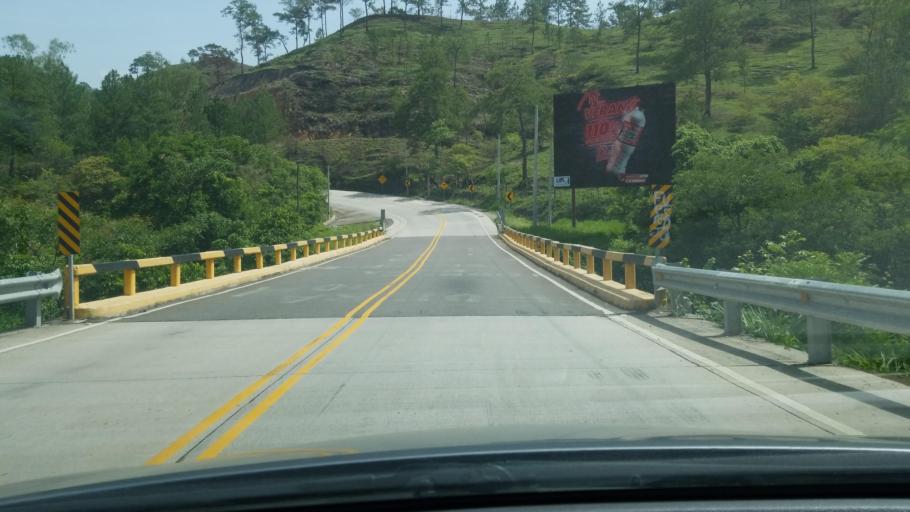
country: HN
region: Copan
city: Florida
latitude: 15.0126
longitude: -88.8340
